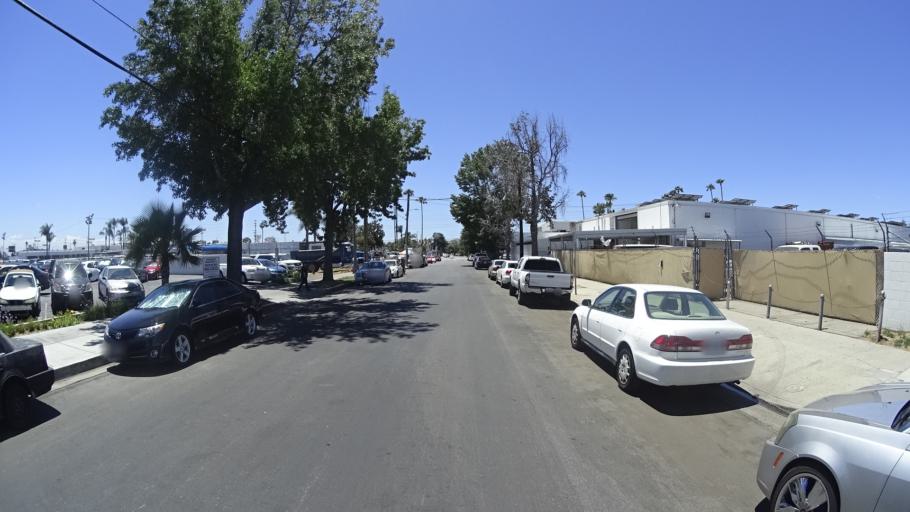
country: US
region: California
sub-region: Los Angeles County
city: Van Nuys
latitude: 34.2228
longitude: -118.4699
